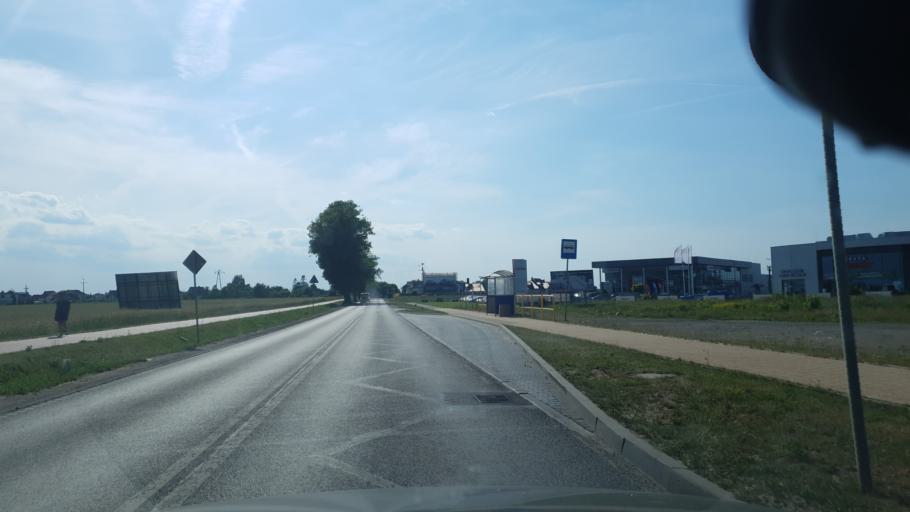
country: PL
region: Pomeranian Voivodeship
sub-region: Powiat kartuski
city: Chwaszczyno
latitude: 54.4426
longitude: 18.4310
